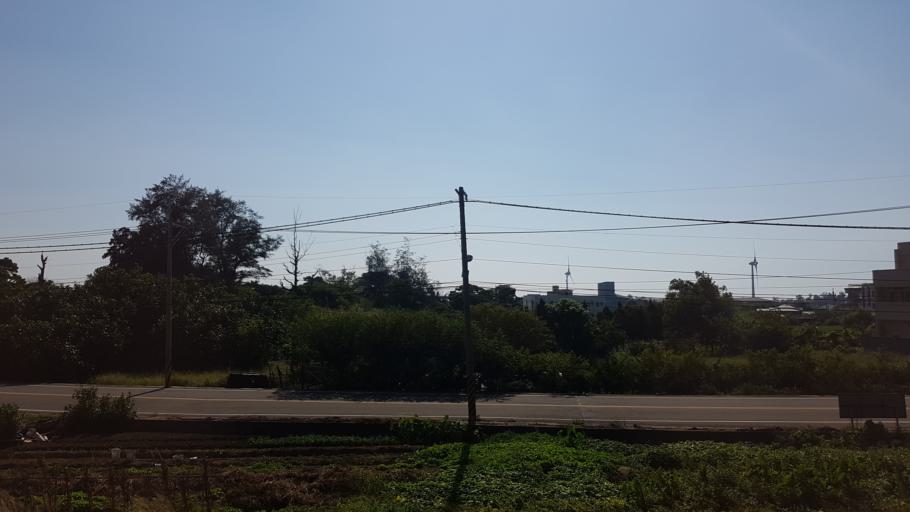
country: TW
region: Taiwan
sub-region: Hsinchu
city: Hsinchu
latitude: 24.7076
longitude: 120.8709
